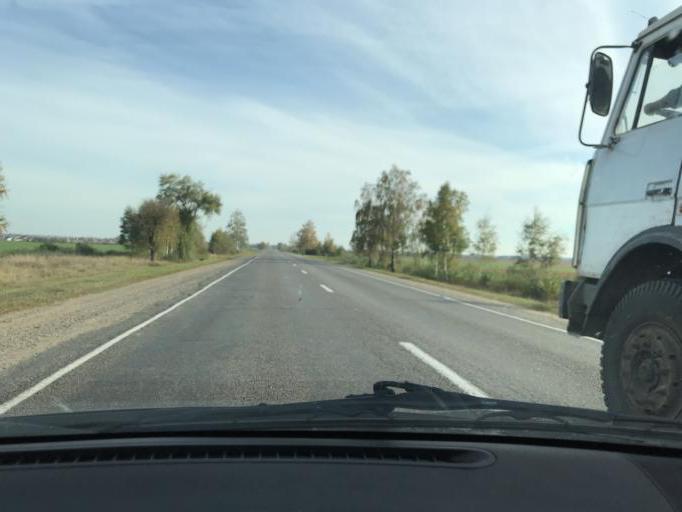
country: BY
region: Brest
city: Asnyezhytsy
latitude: 52.2113
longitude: 26.0470
